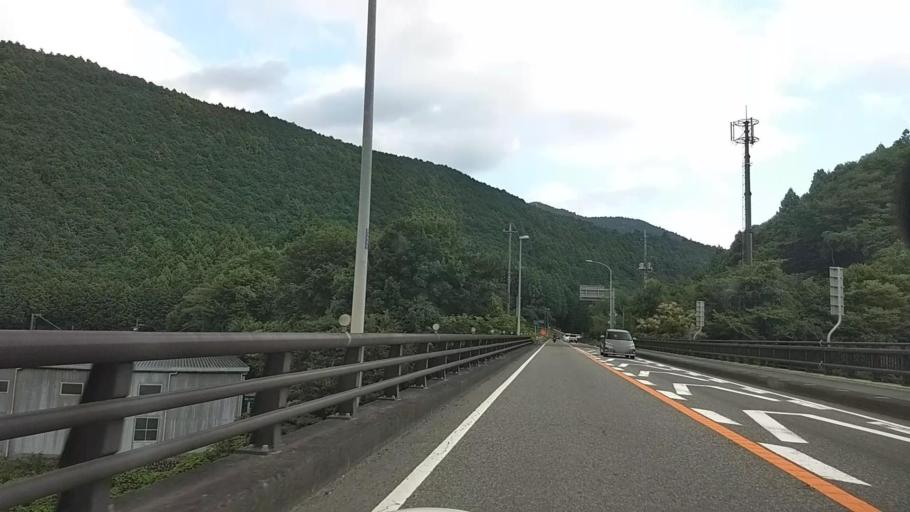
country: JP
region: Shizuoka
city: Fujinomiya
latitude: 35.2249
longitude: 138.5183
